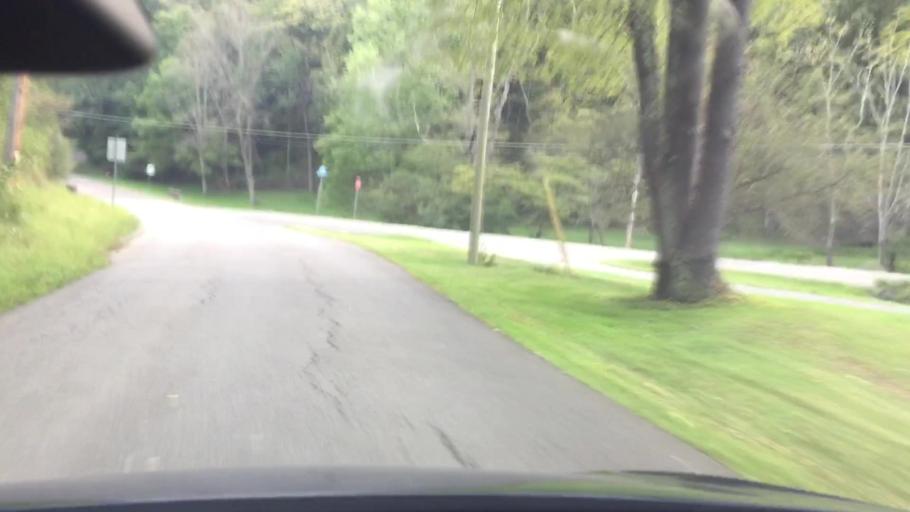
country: US
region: Pennsylvania
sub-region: Allegheny County
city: Curtisville
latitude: 40.6853
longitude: -79.8788
